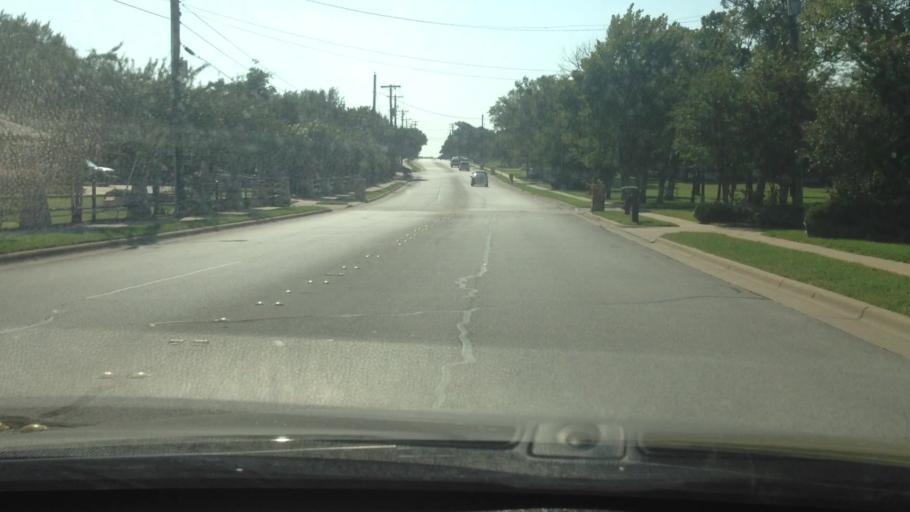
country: US
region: Texas
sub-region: Tarrant County
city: Colleyville
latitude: 32.8840
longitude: -97.1930
